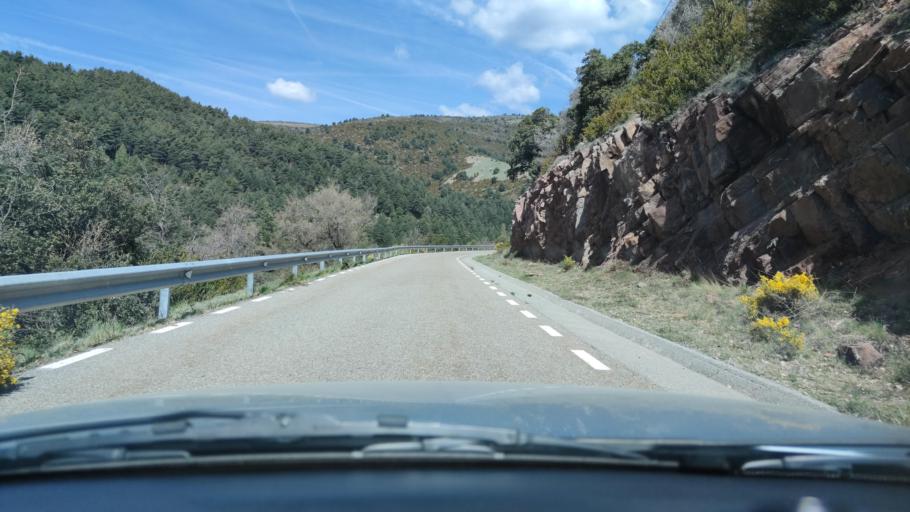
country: ES
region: Catalonia
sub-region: Provincia de Lleida
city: Coll de Nargo
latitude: 42.2909
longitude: 1.2497
